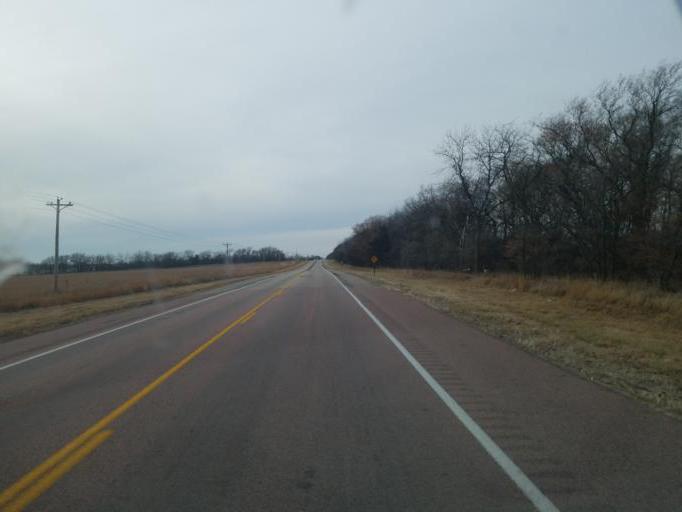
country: US
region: Nebraska
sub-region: Antelope County
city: Neligh
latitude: 42.3353
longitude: -98.1294
